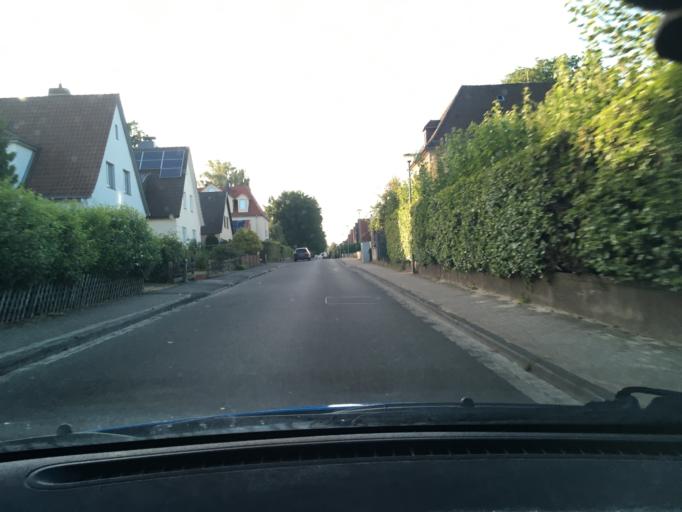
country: DE
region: Lower Saxony
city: Celle
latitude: 52.6306
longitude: 10.0988
